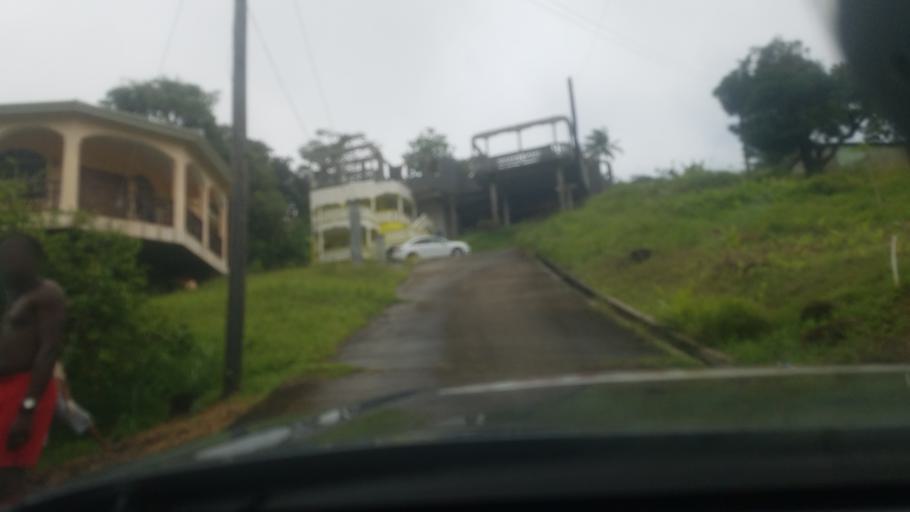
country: LC
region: Gros-Islet
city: Gros Islet
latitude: 14.0323
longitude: -60.9322
